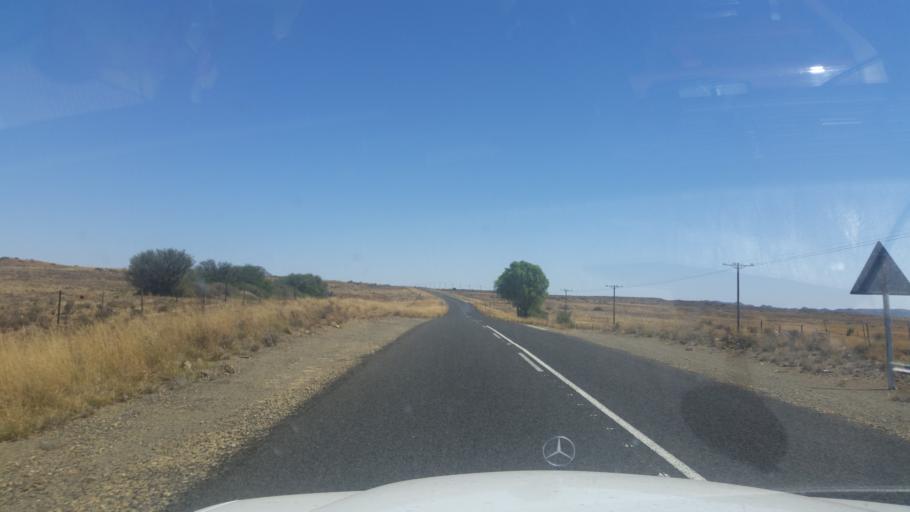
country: ZA
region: Northern Cape
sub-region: Pixley ka Seme District Municipality
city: Colesberg
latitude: -30.7014
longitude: 25.1871
